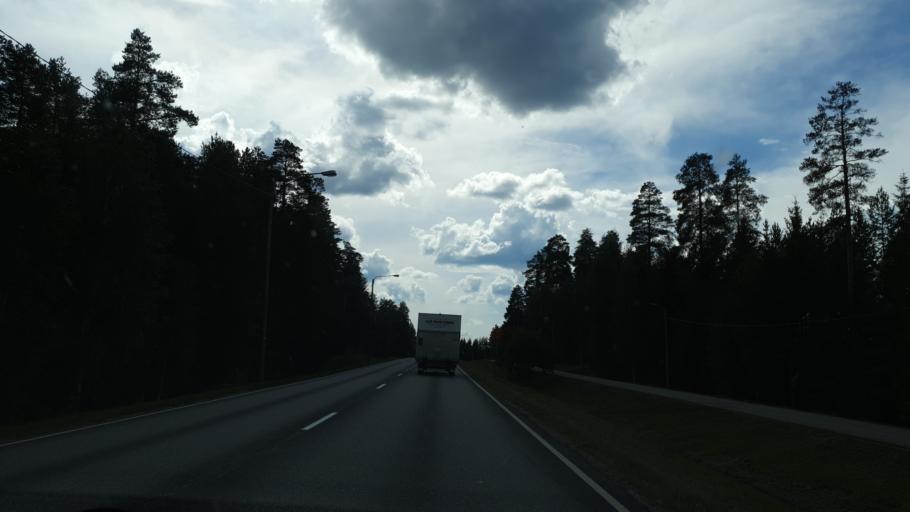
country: FI
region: Kainuu
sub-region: Kajaani
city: Sotkamo
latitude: 64.1396
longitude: 28.4143
